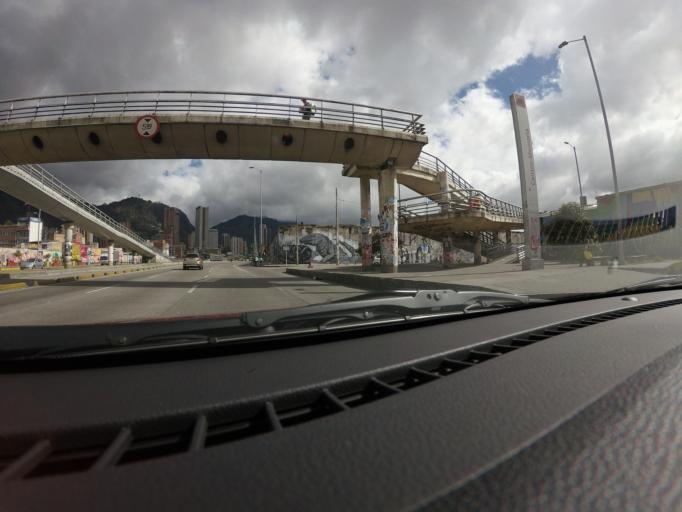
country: CO
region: Bogota D.C.
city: Bogota
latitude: 4.6210
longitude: -74.0773
